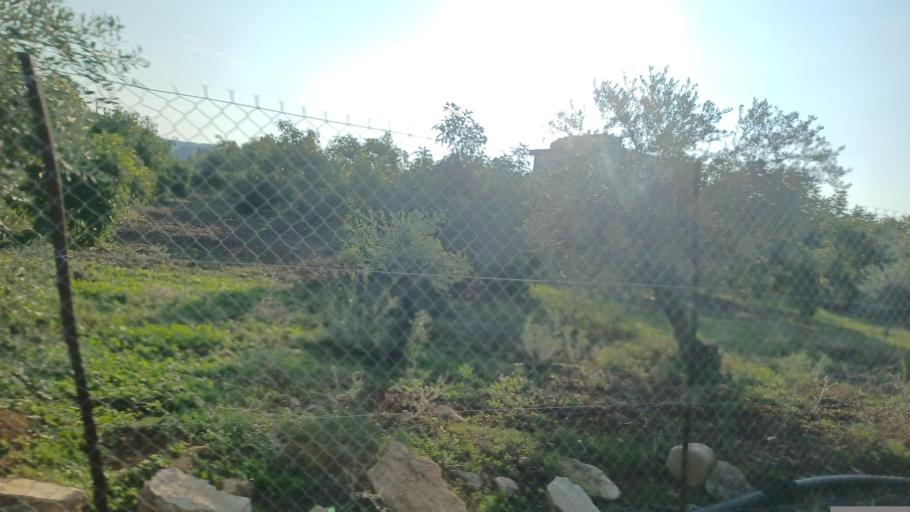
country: CY
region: Pafos
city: Pegeia
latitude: 34.9049
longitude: 32.3327
